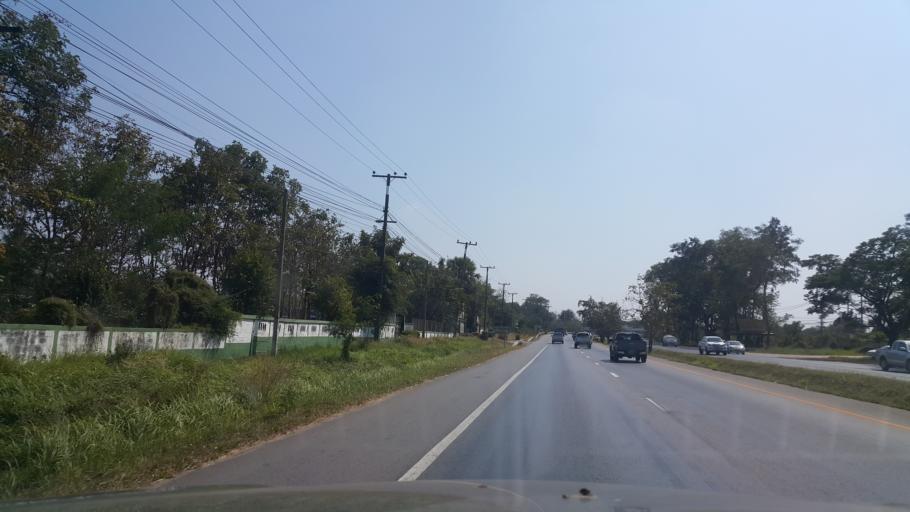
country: TH
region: Khon Kaen
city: Khon Kaen
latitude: 16.5402
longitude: 102.8300
